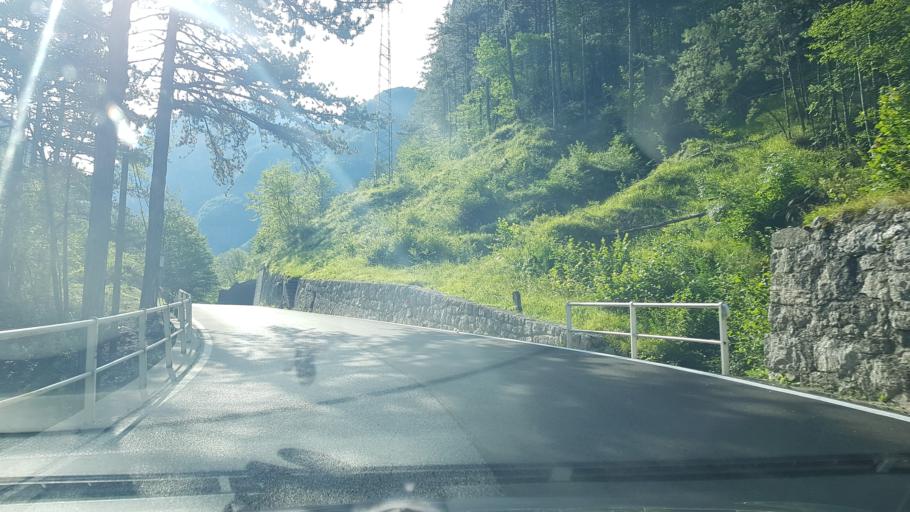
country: IT
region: Friuli Venezia Giulia
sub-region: Provincia di Udine
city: Chiusaforte
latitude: 46.3996
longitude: 13.3202
